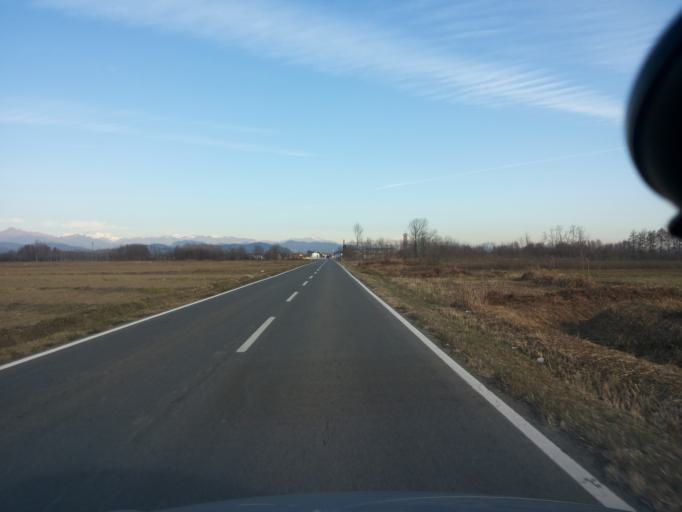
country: IT
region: Piedmont
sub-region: Provincia di Vercelli
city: Lenta
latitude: 45.5441
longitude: 8.3850
